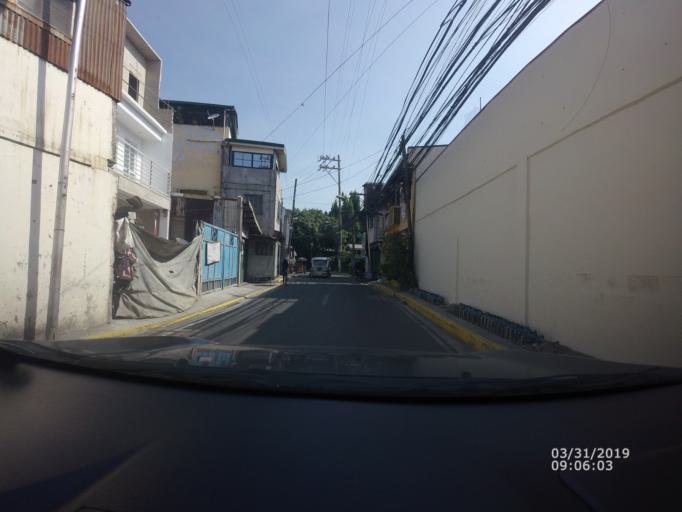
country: PH
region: Metro Manila
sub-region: San Juan
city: San Juan
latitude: 14.5849
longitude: 121.0213
